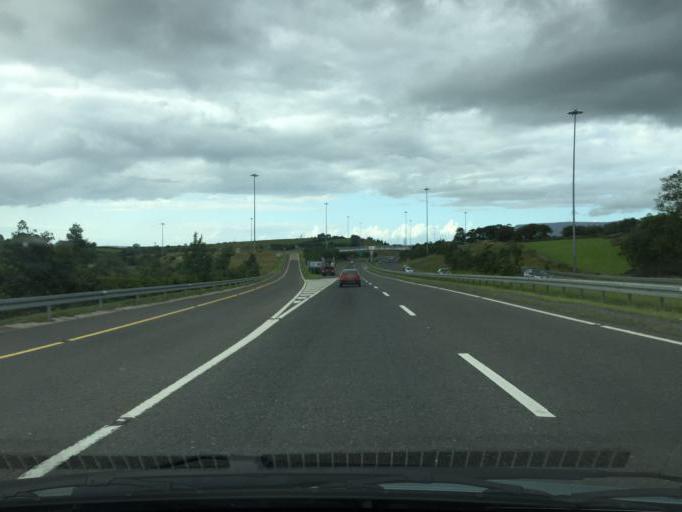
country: IE
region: Connaught
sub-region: Sligo
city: Sligo
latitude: 54.2568
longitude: -8.4789
